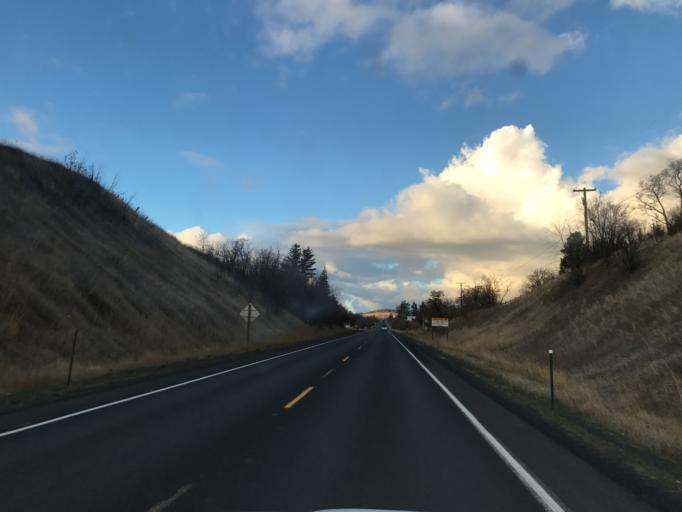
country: US
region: Idaho
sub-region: Latah County
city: Moscow
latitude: 46.7539
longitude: -117.0016
